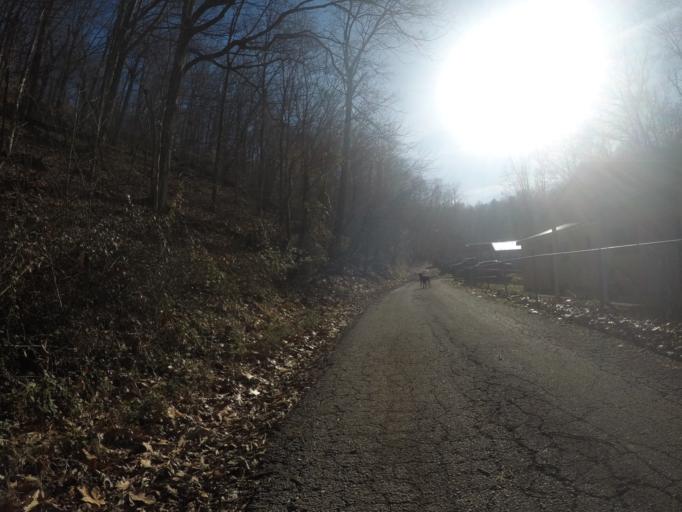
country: US
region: Ohio
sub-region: Lawrence County
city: Burlington
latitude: 38.3933
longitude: -82.4977
